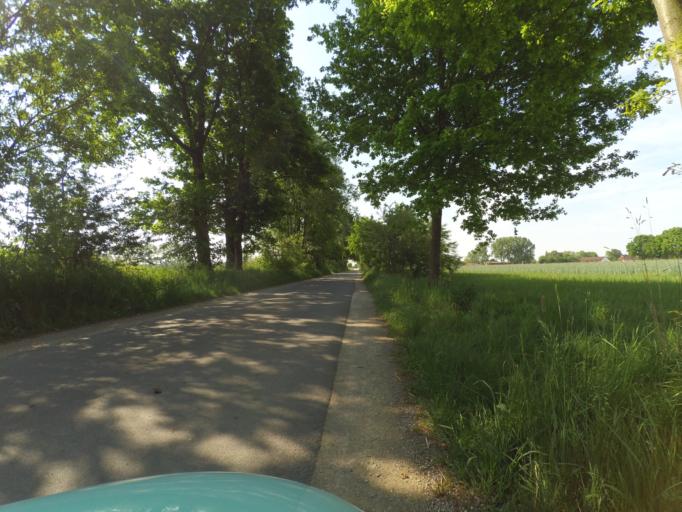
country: DE
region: Lower Saxony
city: Burgdorf
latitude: 52.4374
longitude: 10.0360
